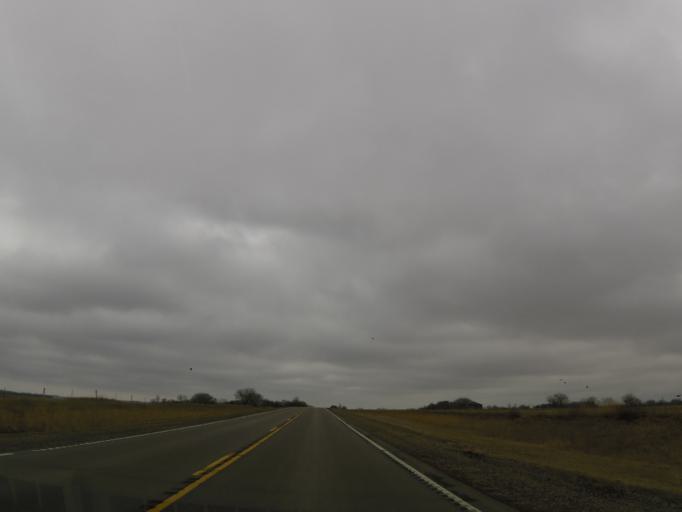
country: US
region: North Dakota
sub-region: Cass County
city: Horace
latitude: 46.6298
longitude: -97.1242
